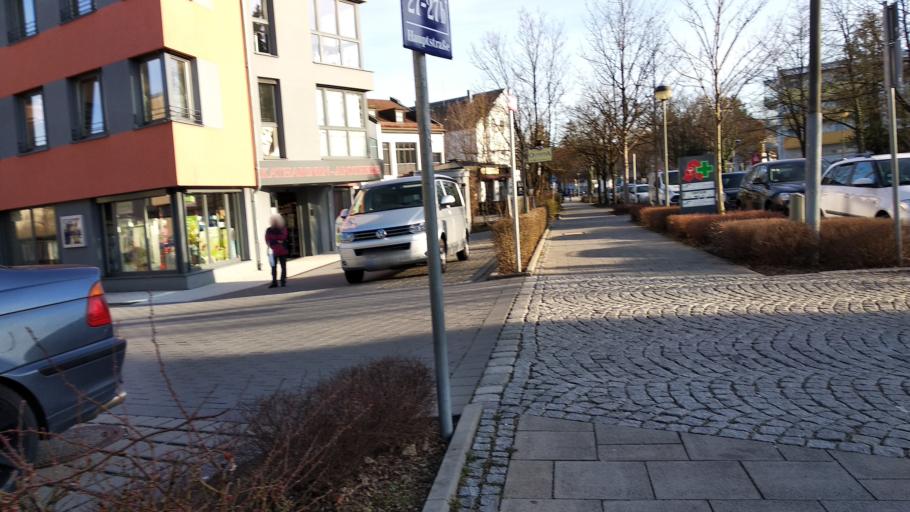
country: DE
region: Bavaria
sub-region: Upper Bavaria
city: Unterhaching
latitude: 48.0633
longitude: 11.6143
